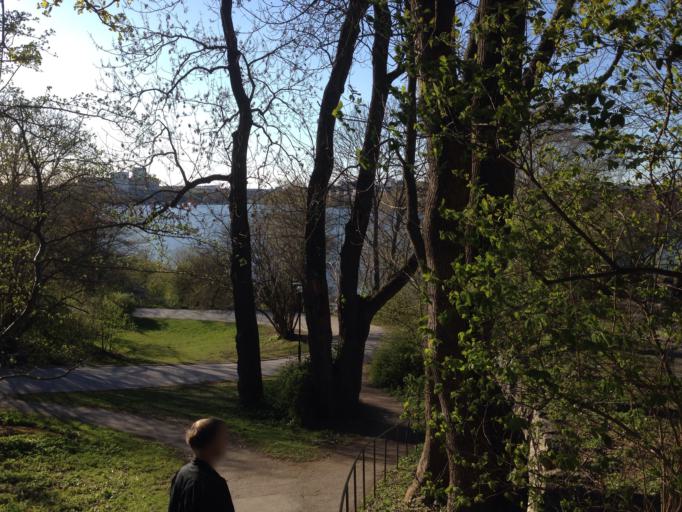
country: SE
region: Stockholm
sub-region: Stockholms Kommun
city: Stockholm
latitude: 59.3202
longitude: 18.0494
